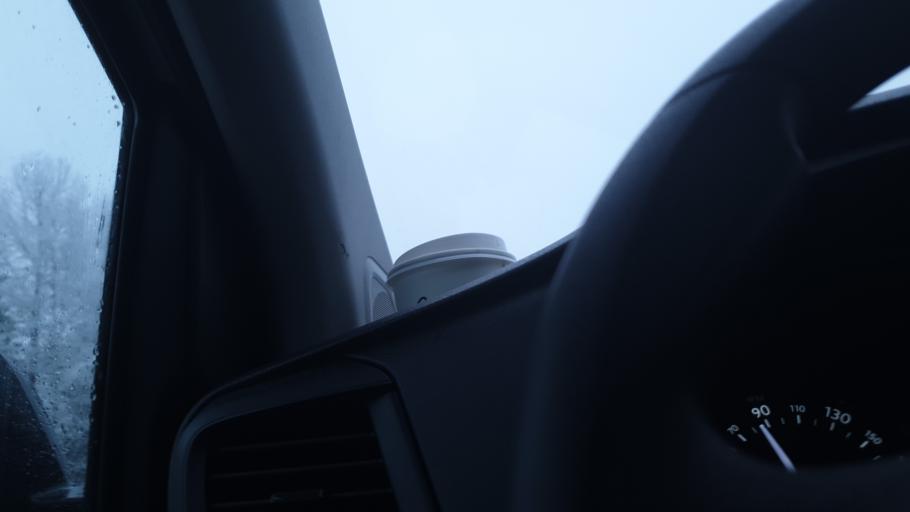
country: FI
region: Central Finland
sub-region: Saarijaervi-Viitasaari
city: Viitasaari
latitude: 62.8777
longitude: 25.8100
